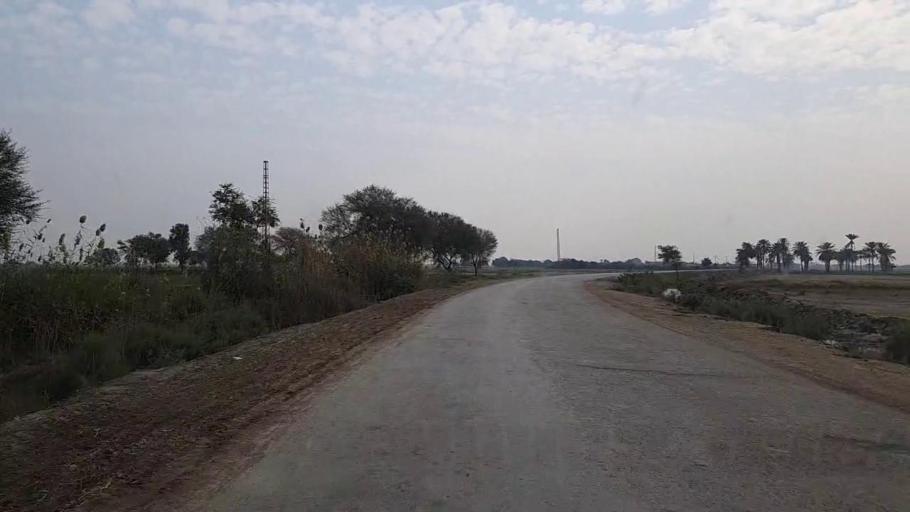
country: PK
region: Sindh
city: Mirwah Gorchani
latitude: 25.3902
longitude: 69.0817
